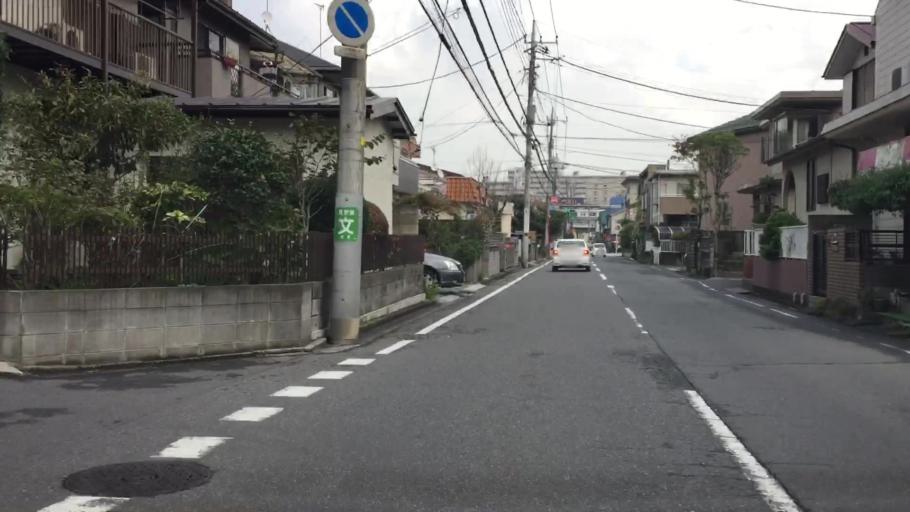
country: JP
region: Chiba
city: Kashiwa
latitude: 35.8367
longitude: 139.9650
